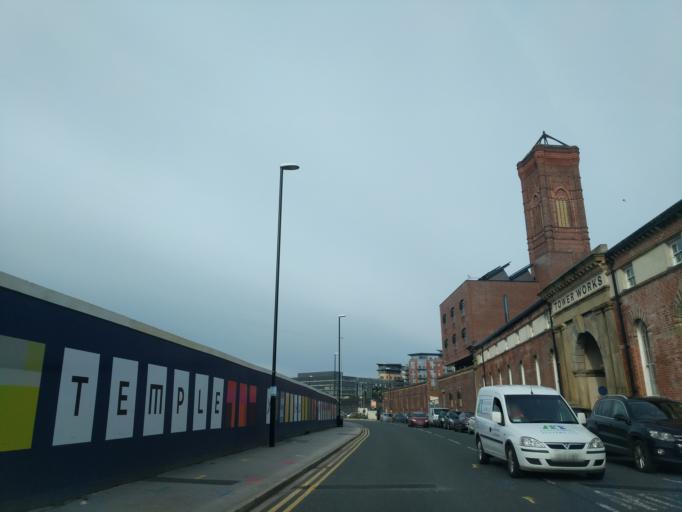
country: GB
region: England
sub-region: City and Borough of Leeds
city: Leeds
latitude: 53.7921
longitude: -1.5520
